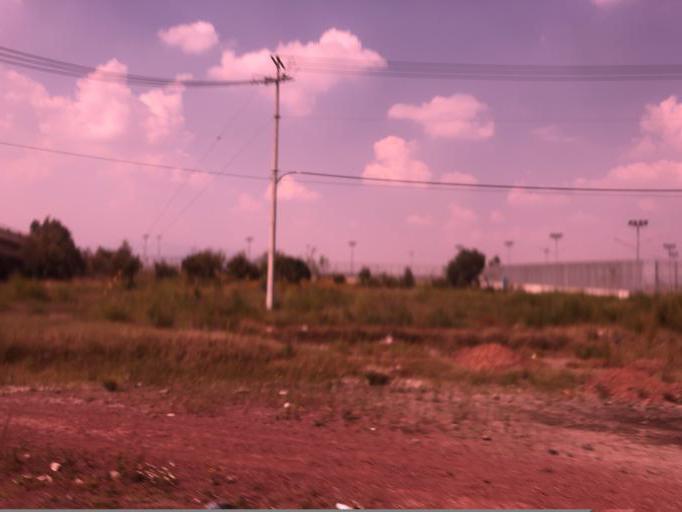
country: MX
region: Mexico
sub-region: Ciudad Nezahualcoyotl
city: Colonia Gustavo Baz Prada
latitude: 19.4707
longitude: -99.0013
